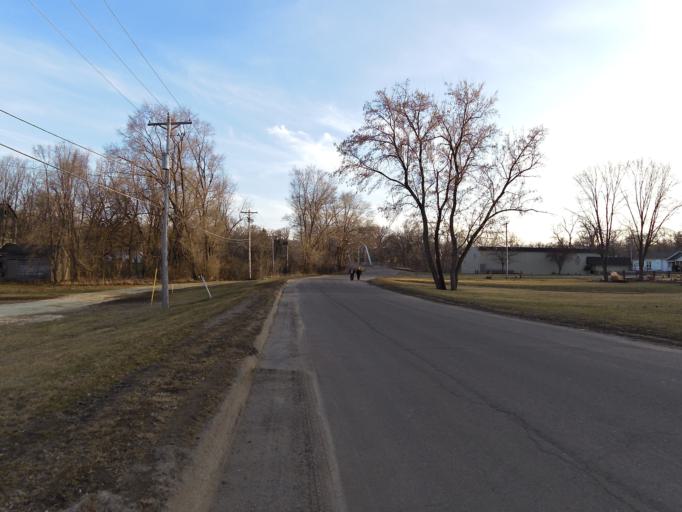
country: US
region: Minnesota
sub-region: Goodhue County
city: Cannon Falls
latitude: 44.5149
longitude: -92.9040
